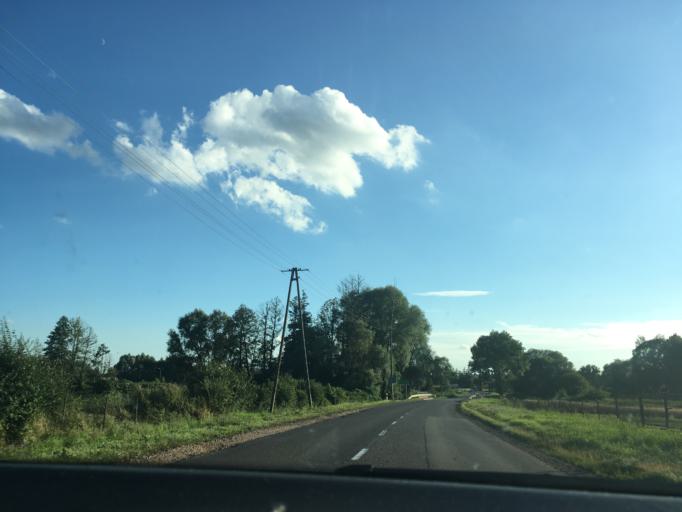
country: PL
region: Masovian Voivodeship
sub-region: Powiat losicki
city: Losice
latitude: 52.2449
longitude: 22.7812
